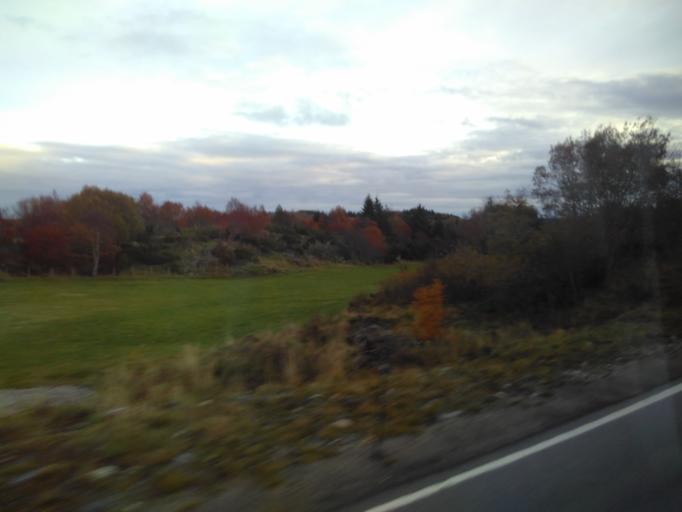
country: NO
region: Sor-Trondelag
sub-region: Froya
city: Sistranda
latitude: 63.6356
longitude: 8.8293
